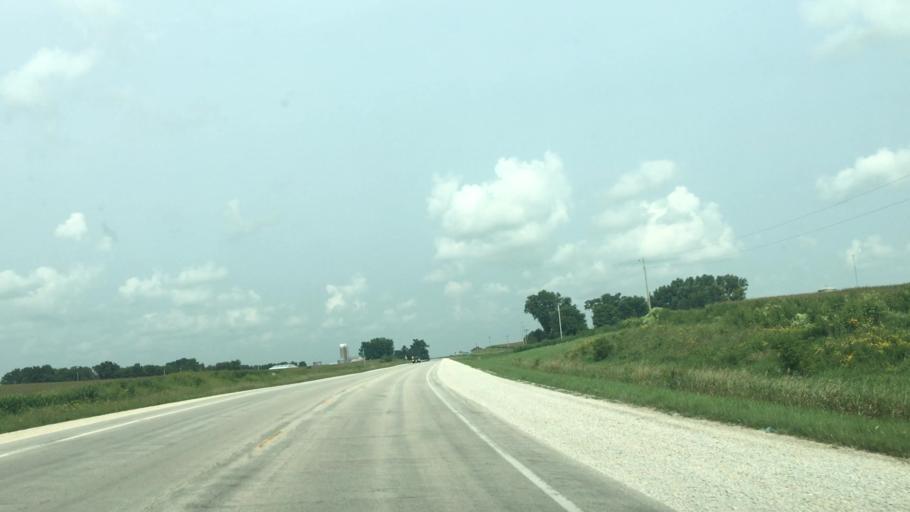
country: US
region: Iowa
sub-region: Winneshiek County
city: Decorah
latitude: 43.4070
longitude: -91.8545
